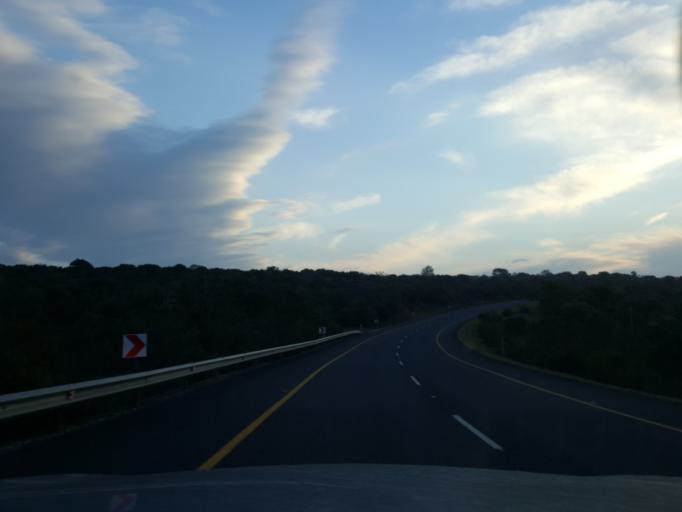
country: ZA
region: Eastern Cape
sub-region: Cacadu District Municipality
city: Grahamstown
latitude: -33.3796
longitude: 26.4630
